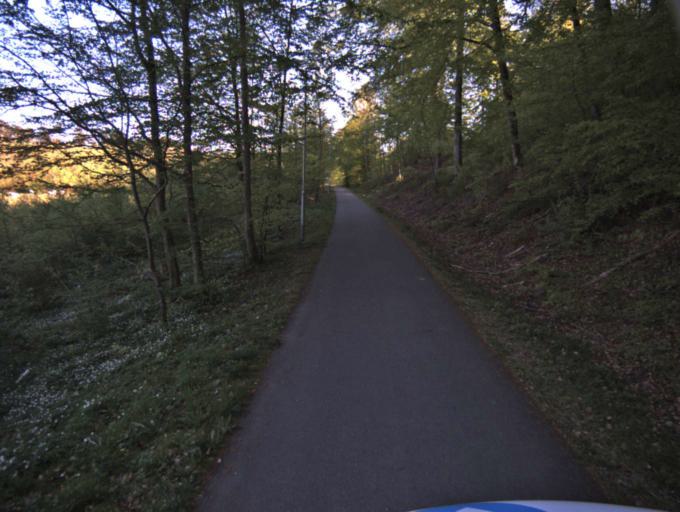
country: SE
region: Skane
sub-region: Kristianstads Kommun
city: Degeberga
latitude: 55.8345
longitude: 14.0791
